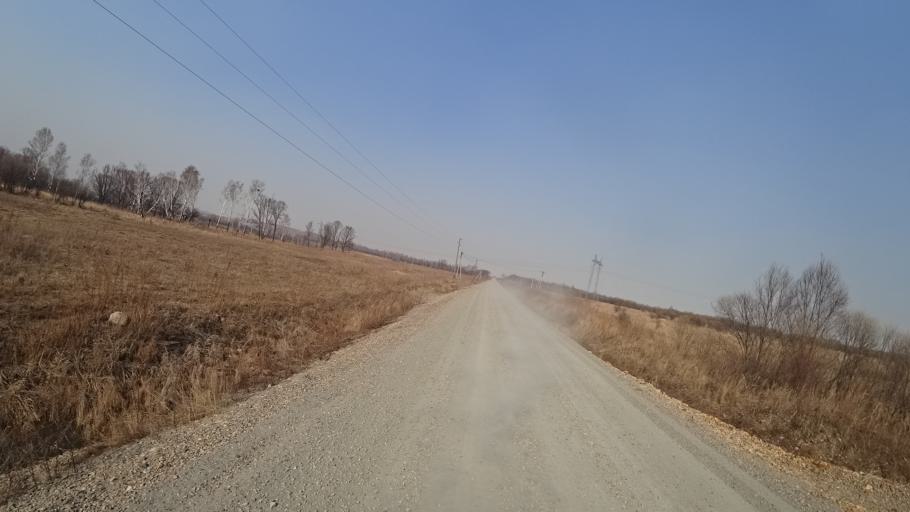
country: RU
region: Amur
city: Novobureyskiy
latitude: 49.8131
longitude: 129.9723
